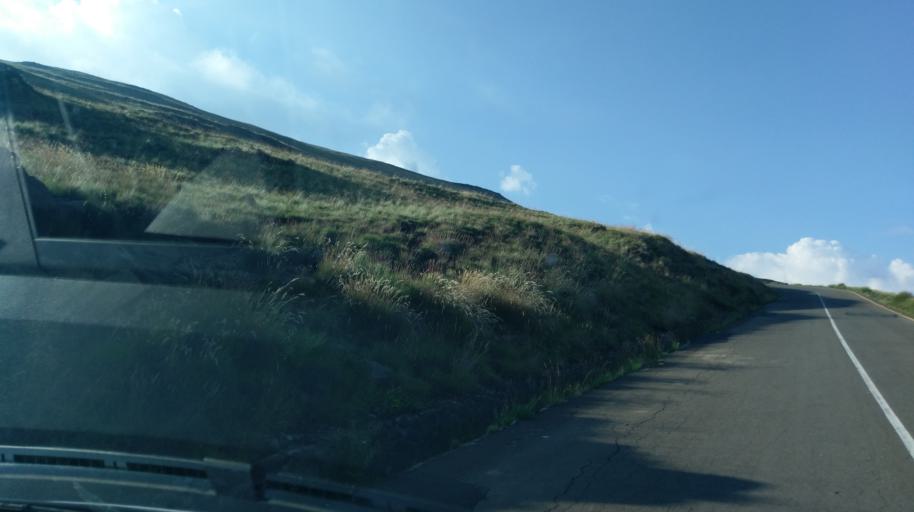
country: LS
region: Butha-Buthe
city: Butha-Buthe
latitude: -29.0781
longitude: 28.4254
